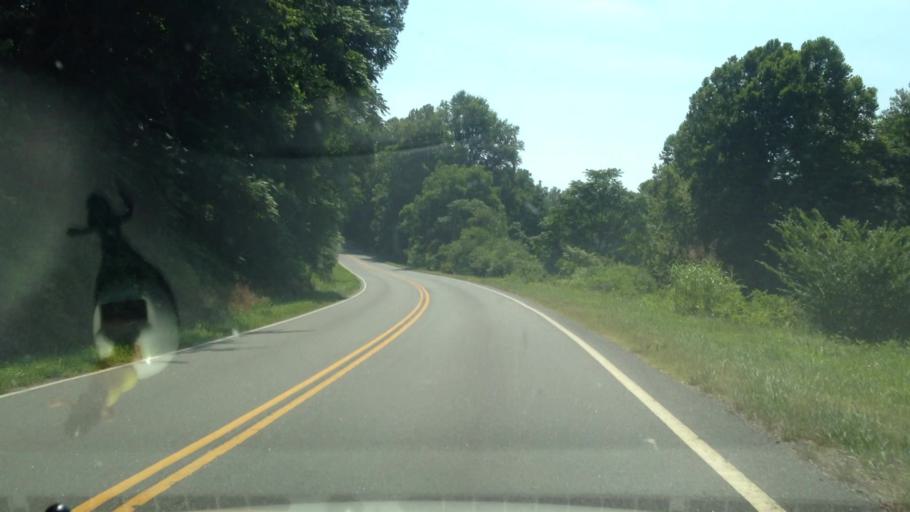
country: US
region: Virginia
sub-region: Patrick County
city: Stuart
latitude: 36.5871
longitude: -80.4036
